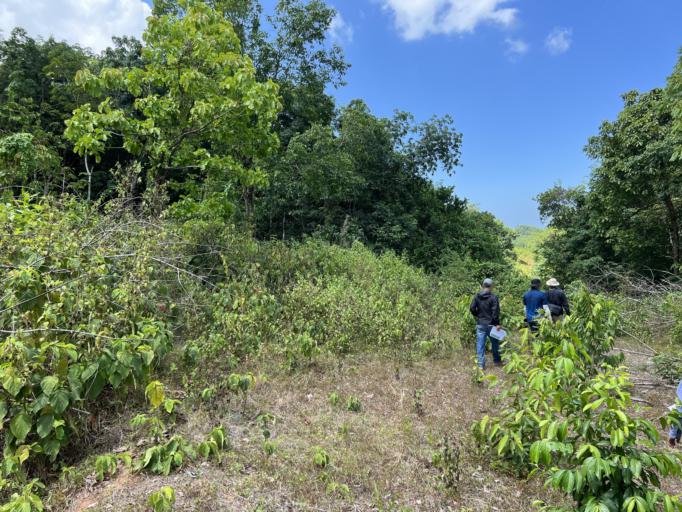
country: MM
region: Tanintharyi
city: Dawei
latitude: 14.5918
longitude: 97.9407
